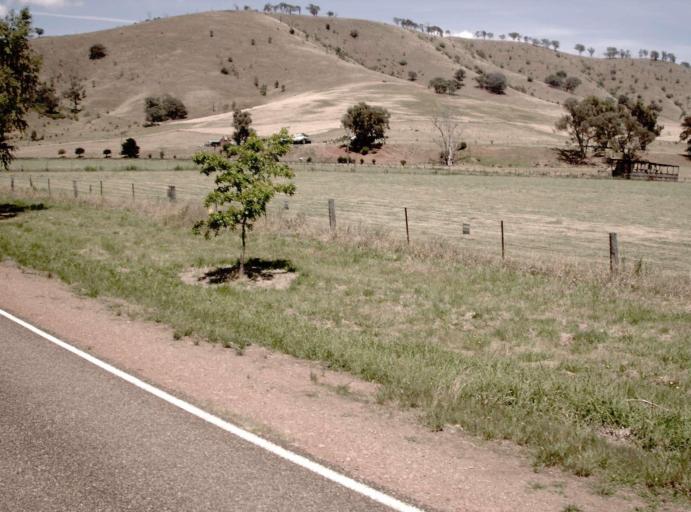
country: AU
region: Victoria
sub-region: East Gippsland
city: Bairnsdale
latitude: -37.2522
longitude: 147.7118
